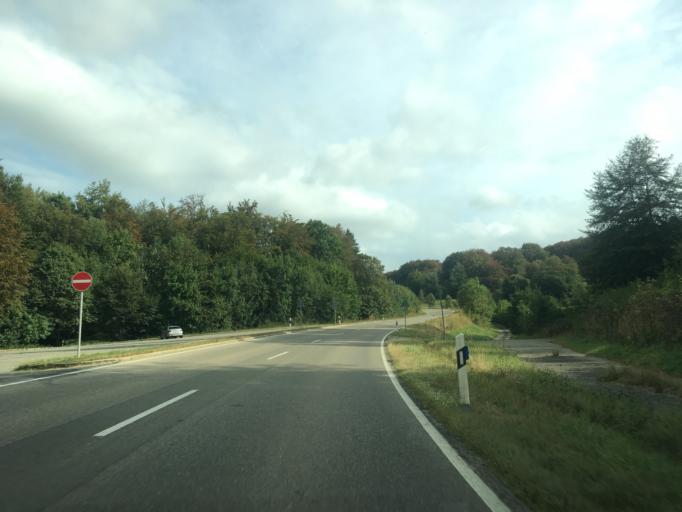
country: DE
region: Baden-Wuerttemberg
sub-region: Tuebingen Region
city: Pfullingen
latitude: 48.4002
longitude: 9.2625
